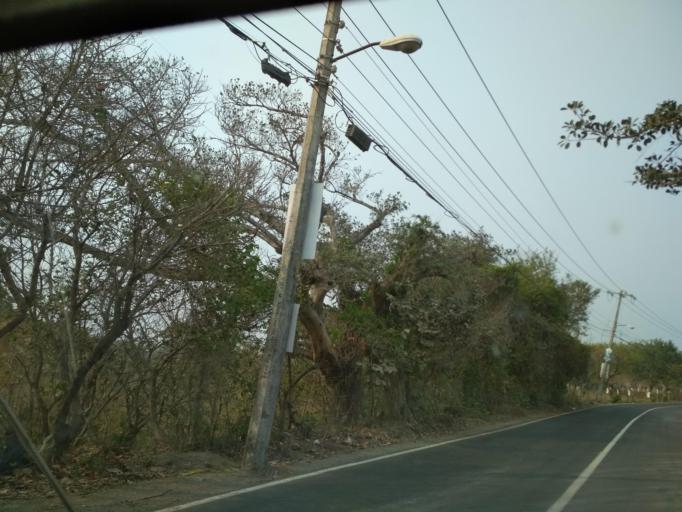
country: MX
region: Veracruz
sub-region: Veracruz
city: Las Amapolas
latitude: 19.1493
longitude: -96.2284
